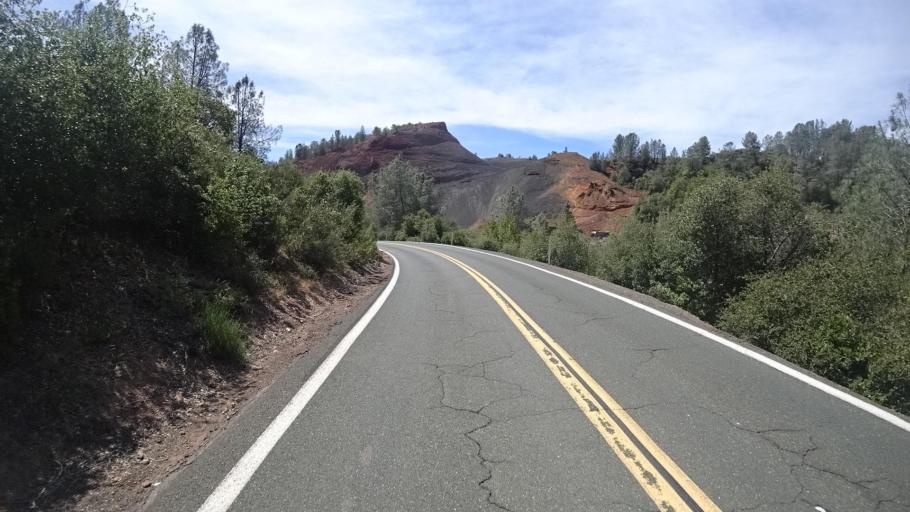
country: US
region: California
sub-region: Lake County
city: Clearlake
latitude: 38.9207
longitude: -122.6650
